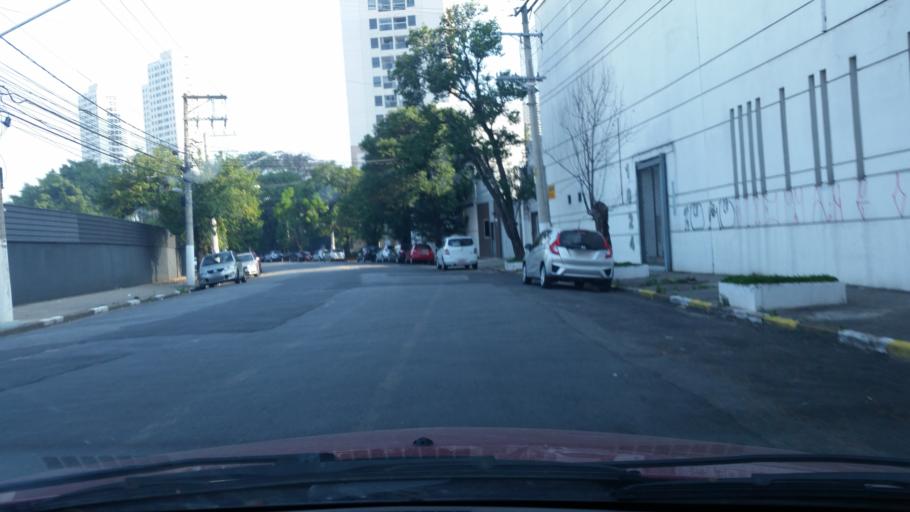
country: BR
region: Sao Paulo
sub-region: Osasco
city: Osasco
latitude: -23.5309
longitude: -46.7445
